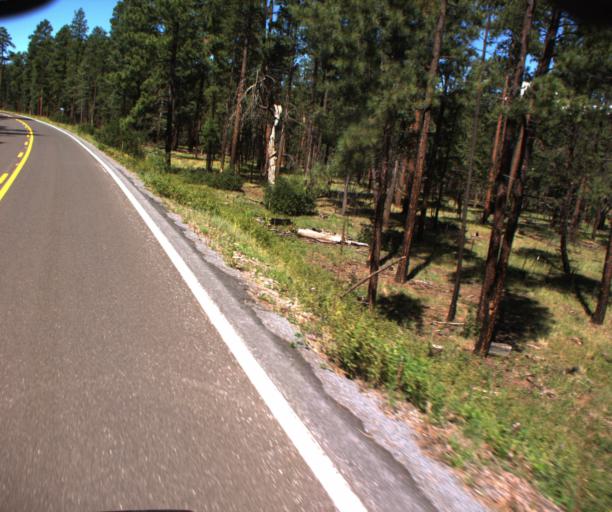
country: US
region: Arizona
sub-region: Apache County
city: Eagar
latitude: 33.6843
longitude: -109.2346
